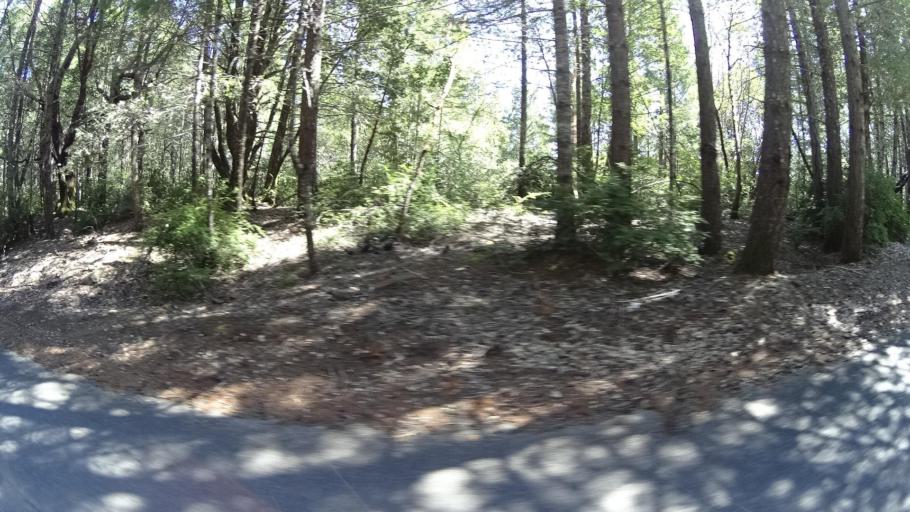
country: US
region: California
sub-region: Humboldt County
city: Redway
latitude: 40.2021
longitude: -124.1017
